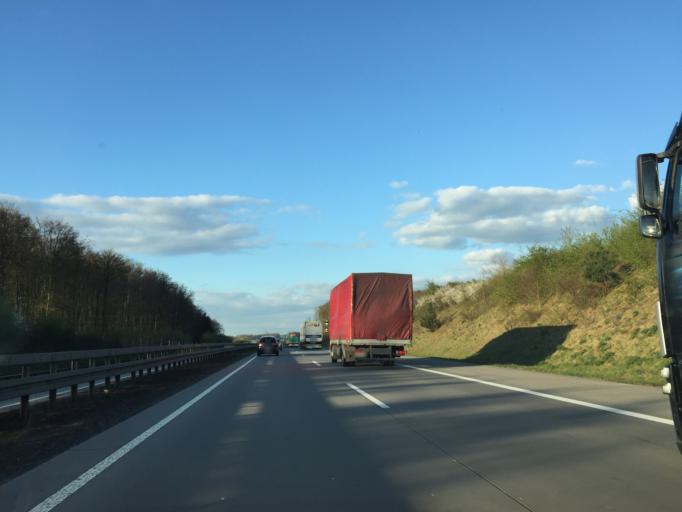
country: DE
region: Hesse
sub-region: Regierungsbezirk Giessen
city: Lich
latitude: 50.5375
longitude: 8.7743
